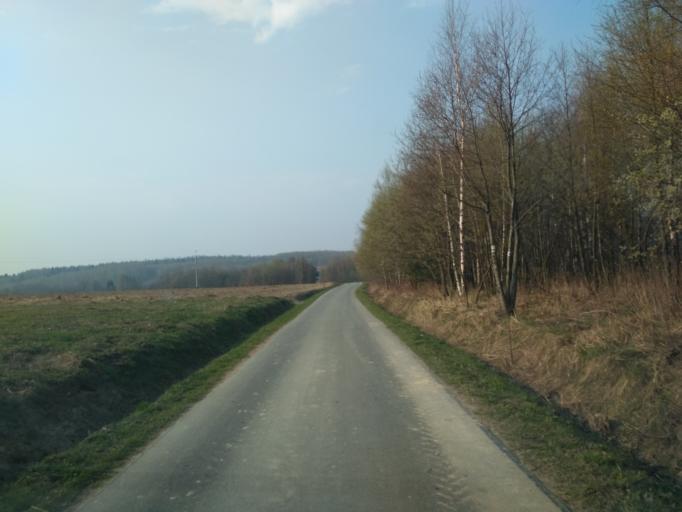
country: PL
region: Subcarpathian Voivodeship
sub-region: Powiat ropczycko-sedziszowski
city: Wielopole Skrzynskie
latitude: 49.9095
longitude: 21.5959
